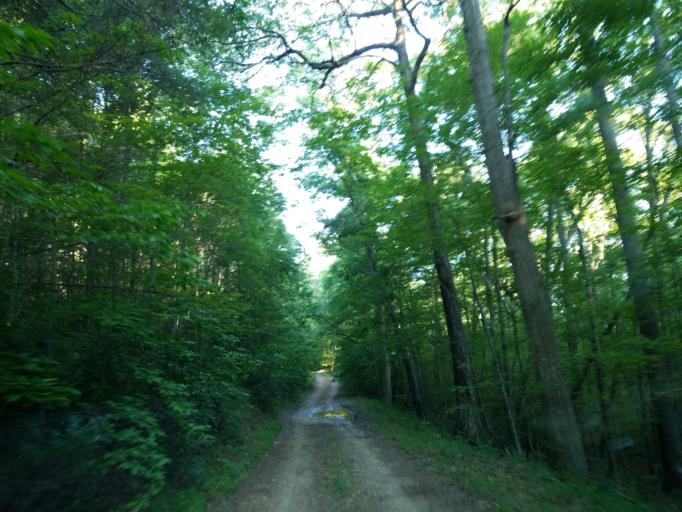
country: US
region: Georgia
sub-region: Fannin County
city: Blue Ridge
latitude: 34.8163
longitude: -84.1500
